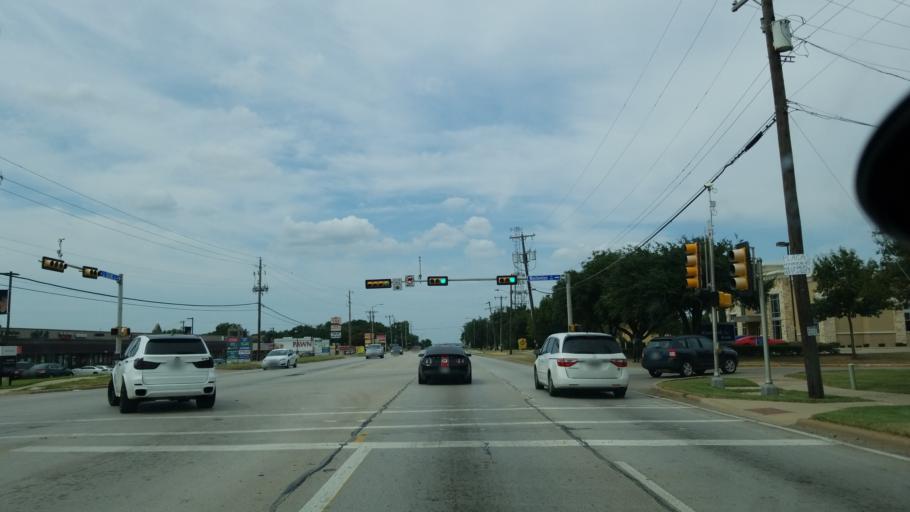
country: US
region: Texas
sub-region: Tarrant County
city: Arlington
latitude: 32.7701
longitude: -97.0970
